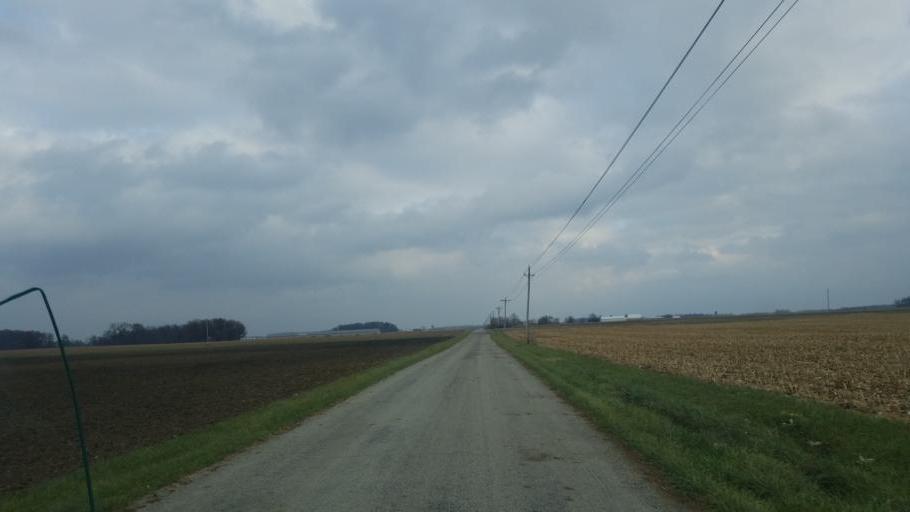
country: US
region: Indiana
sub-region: Adams County
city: Geneva
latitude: 40.5131
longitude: -84.8791
